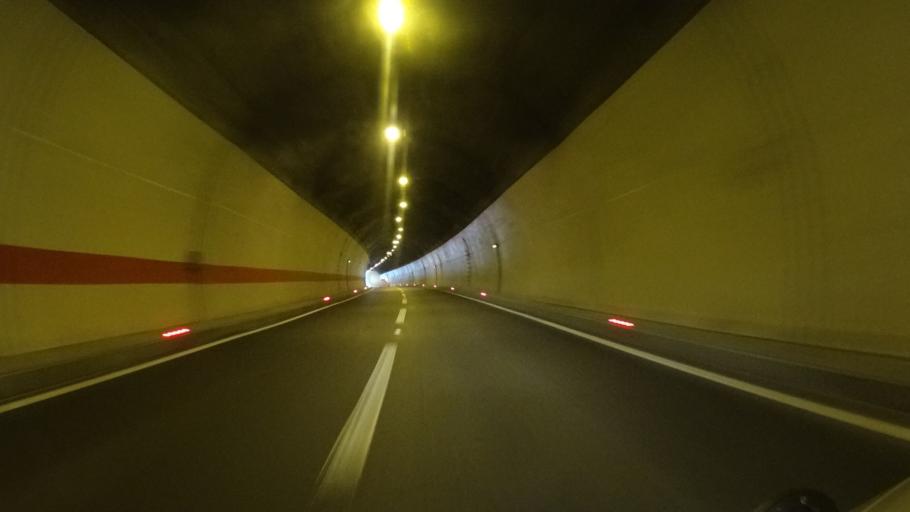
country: HR
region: Varazdinska
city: Ljubescica
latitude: 46.2228
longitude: 16.4084
